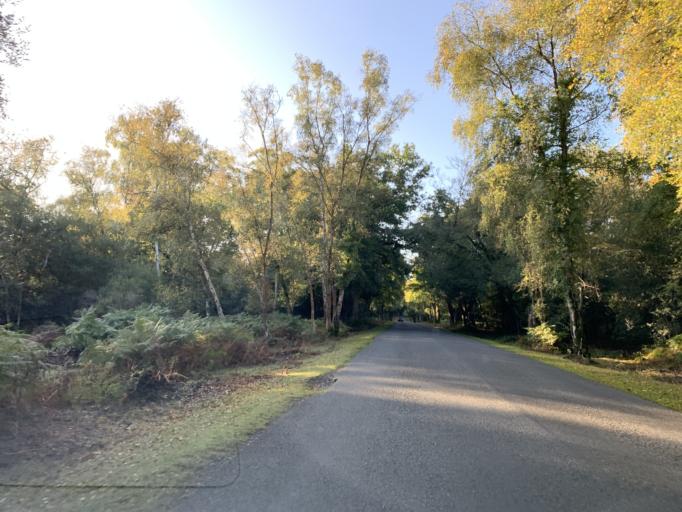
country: GB
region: England
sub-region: Hampshire
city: West Wellow
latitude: 50.9538
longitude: -1.6292
